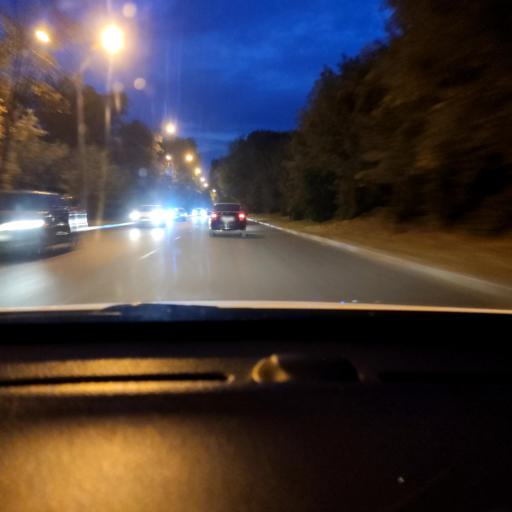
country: RU
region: Voronezj
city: Voronezh
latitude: 51.6640
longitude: 39.2197
